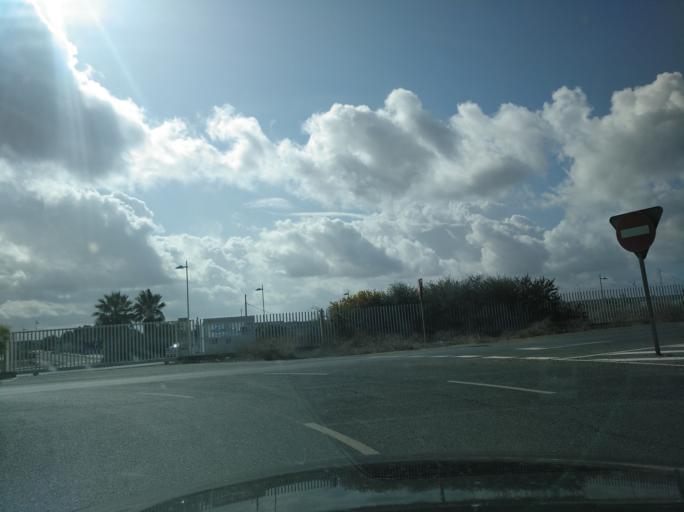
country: ES
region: Andalusia
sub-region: Provincia de Sevilla
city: Umbrete
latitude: 37.3623
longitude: -6.1453
